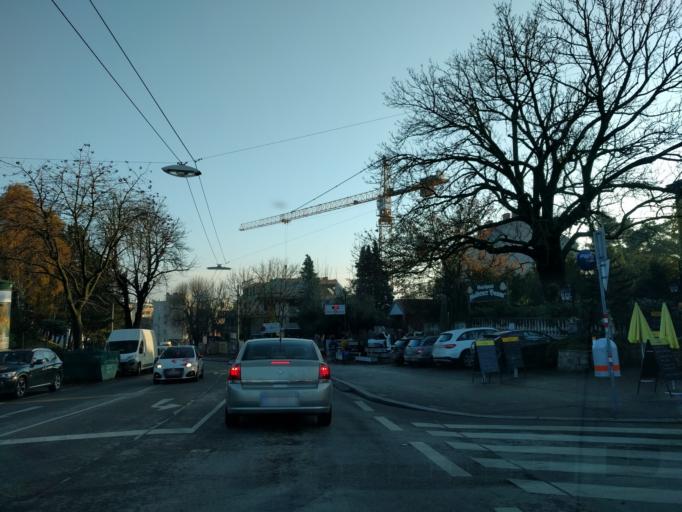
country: AT
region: Lower Austria
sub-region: Politischer Bezirk Modling
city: Perchtoldsdorf
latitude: 48.2001
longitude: 16.2795
